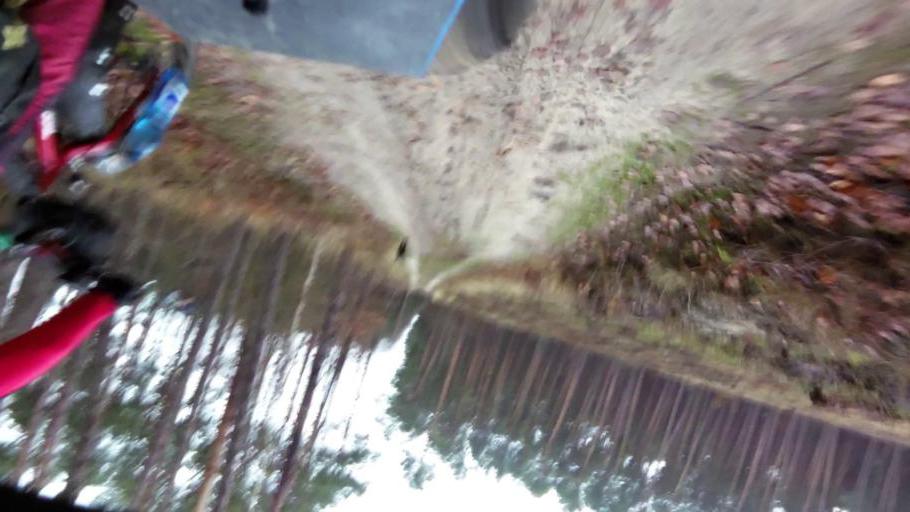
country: PL
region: Lubusz
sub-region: Powiat gorzowski
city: Witnica
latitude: 52.6947
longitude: 14.8144
